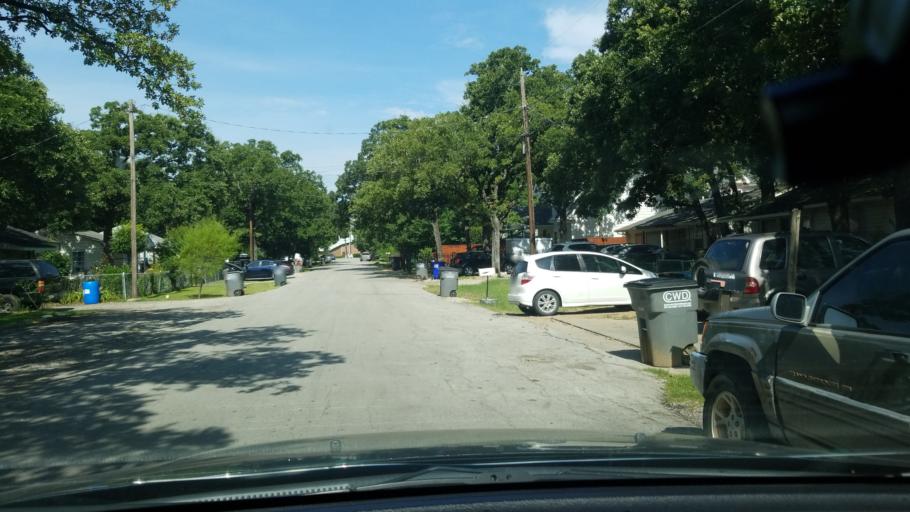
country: US
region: Texas
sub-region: Dallas County
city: Balch Springs
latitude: 32.7189
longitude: -96.6288
